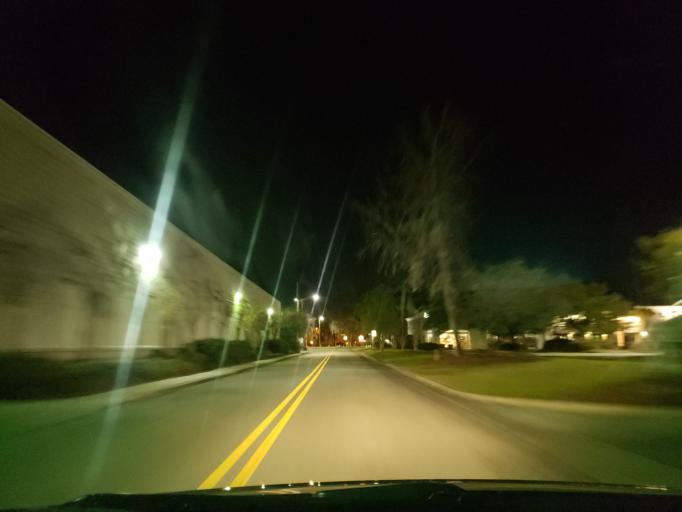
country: US
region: Georgia
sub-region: Chatham County
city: Savannah
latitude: 32.0237
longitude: -81.1112
